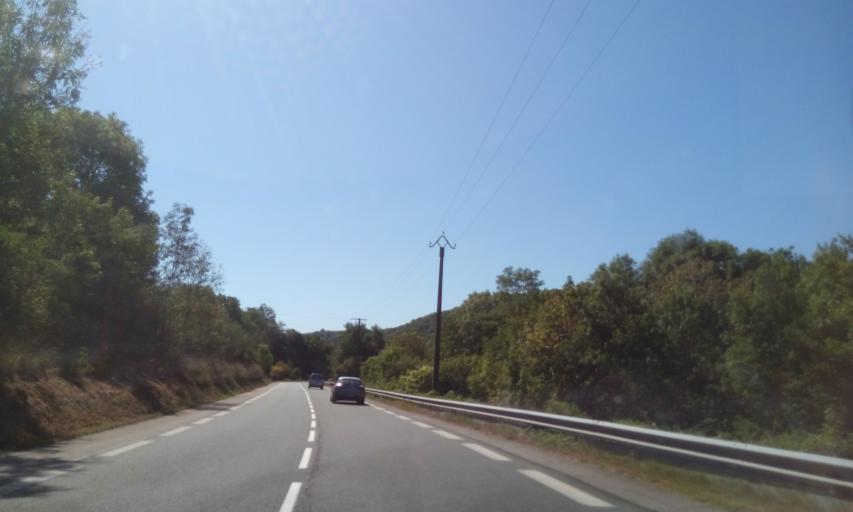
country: FR
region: Rhone-Alpes
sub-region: Departement du Rhone
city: Saint-Verand
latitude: 45.9714
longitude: 4.5089
